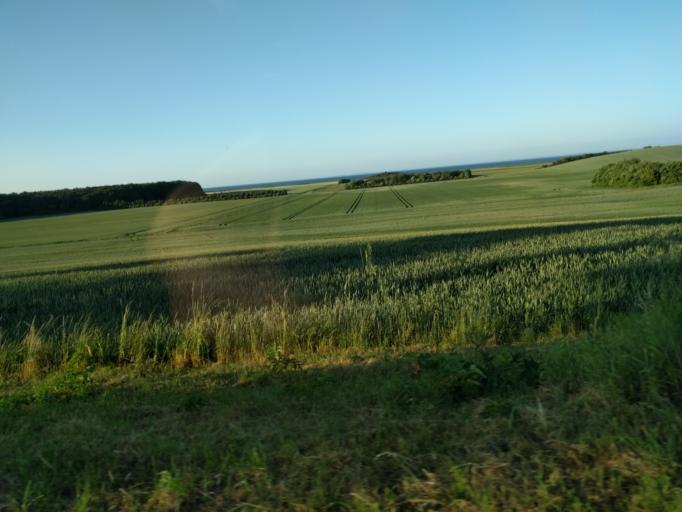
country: DK
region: South Denmark
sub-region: Kerteminde Kommune
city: Kerteminde
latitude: 55.5822
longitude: 10.6376
